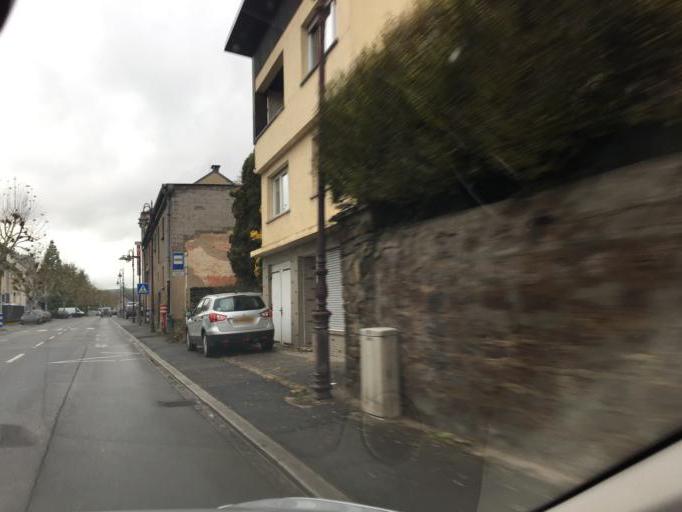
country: LU
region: Diekirch
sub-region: Canton de Diekirch
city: Diekirch
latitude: 49.8688
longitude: 6.1727
